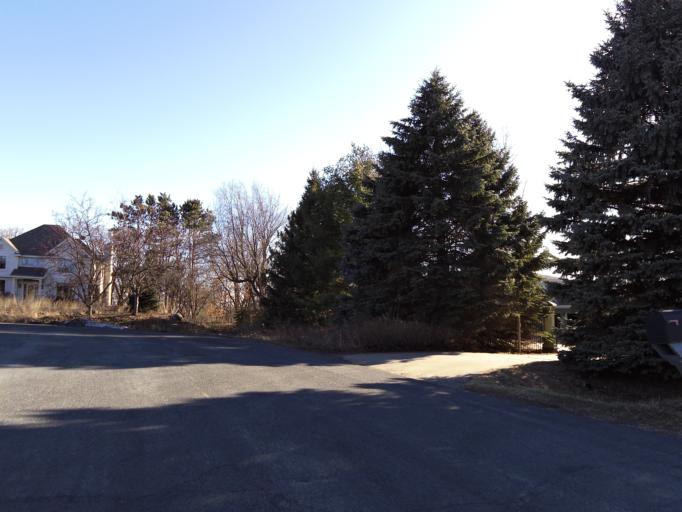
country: US
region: Minnesota
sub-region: Washington County
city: Bayport
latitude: 44.9862
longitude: -92.8070
